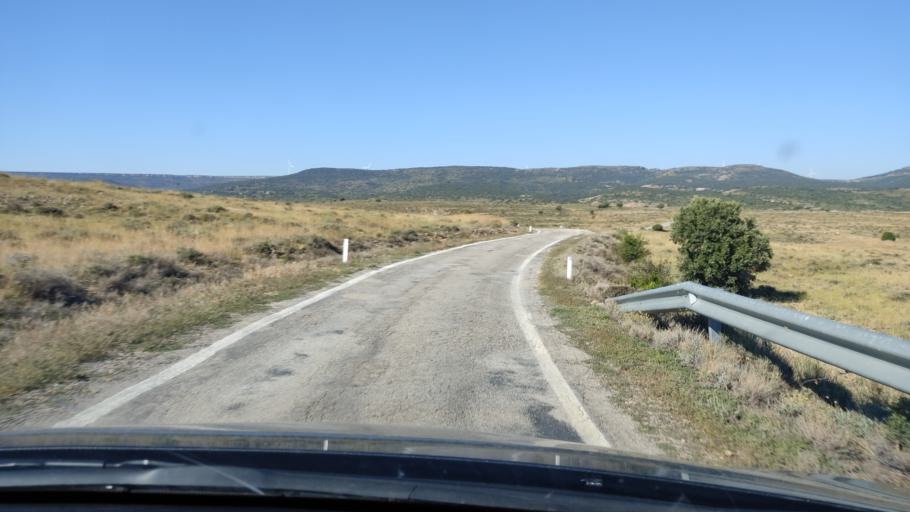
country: ES
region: Aragon
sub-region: Provincia de Teruel
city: Anadon
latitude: 41.0186
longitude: -0.9660
